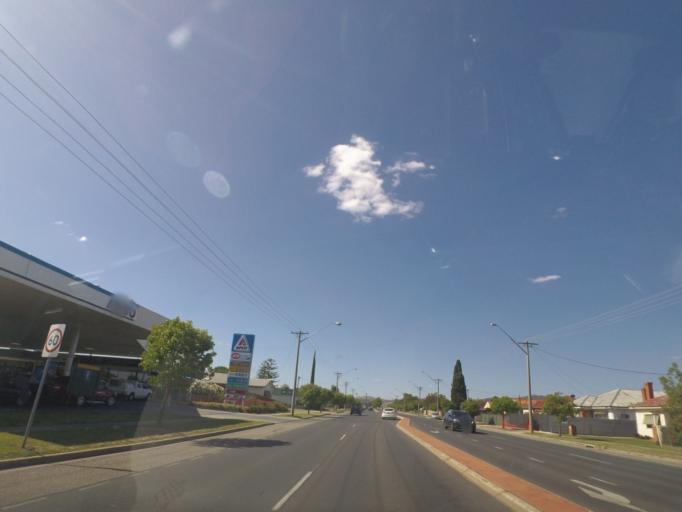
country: AU
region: New South Wales
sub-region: Albury Municipality
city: North Albury
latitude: -36.0575
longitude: 146.9326
